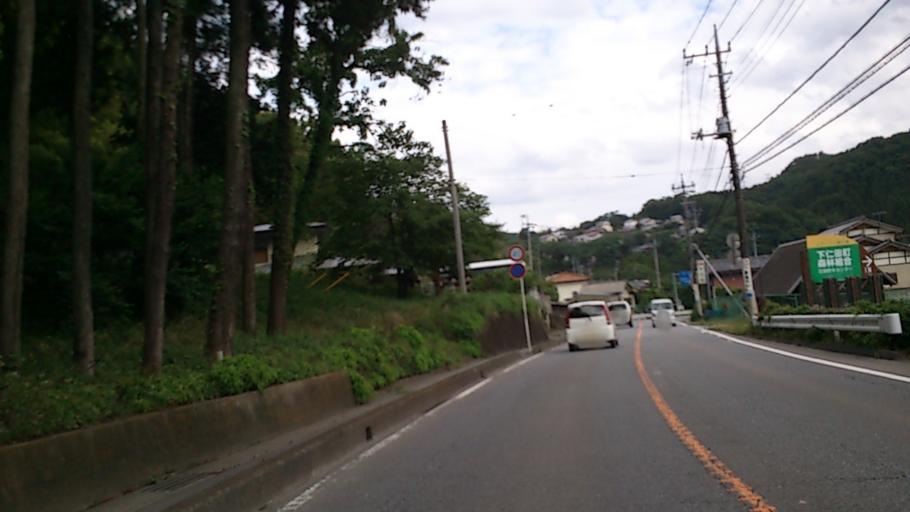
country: JP
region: Gunma
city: Tomioka
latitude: 36.2183
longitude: 138.8016
